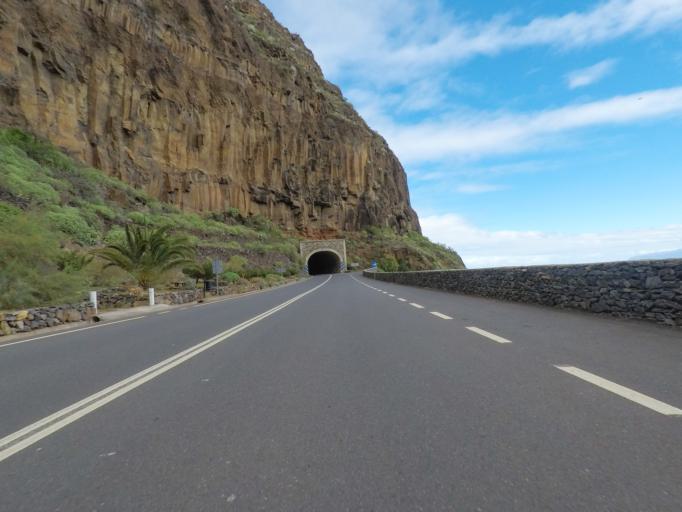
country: ES
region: Canary Islands
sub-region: Provincia de Santa Cruz de Tenerife
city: Agulo
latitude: 28.1905
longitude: -17.1979
